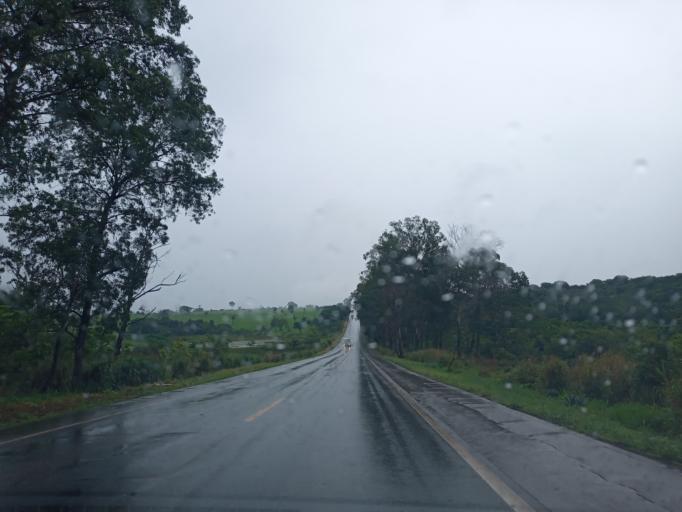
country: BR
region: Minas Gerais
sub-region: Luz
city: Luz
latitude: -19.7839
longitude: -45.7009
